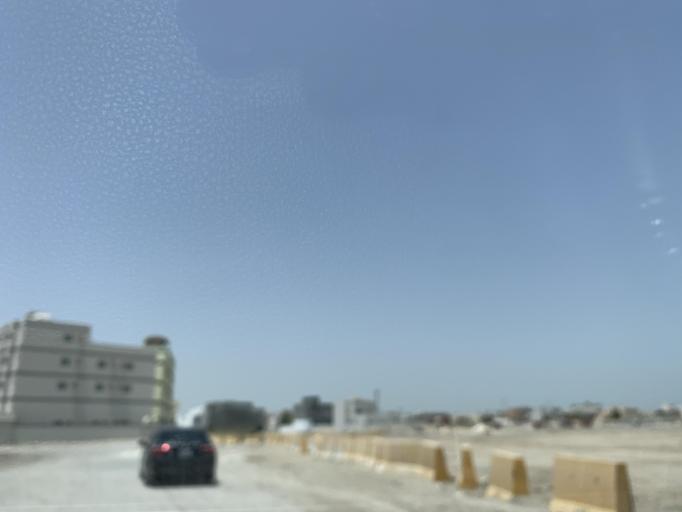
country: BH
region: Northern
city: Sitrah
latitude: 26.1433
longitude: 50.5936
